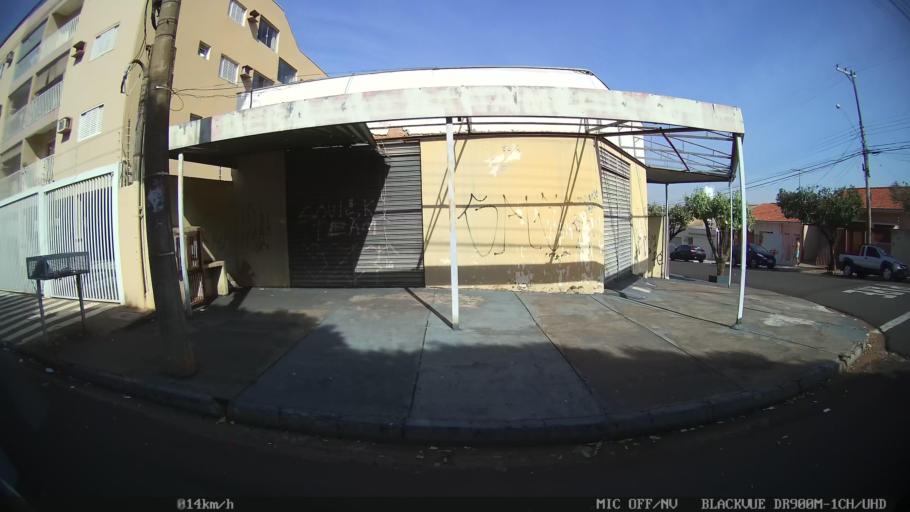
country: BR
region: Sao Paulo
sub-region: Sao Jose Do Rio Preto
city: Sao Jose do Rio Preto
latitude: -20.8014
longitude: -49.4119
